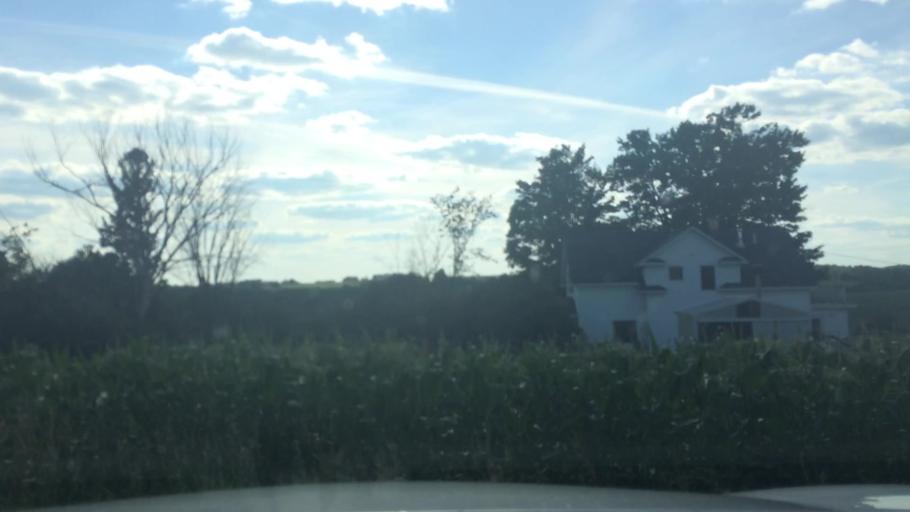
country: US
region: Wisconsin
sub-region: Lincoln County
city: Merrill
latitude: 45.1783
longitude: -89.5848
